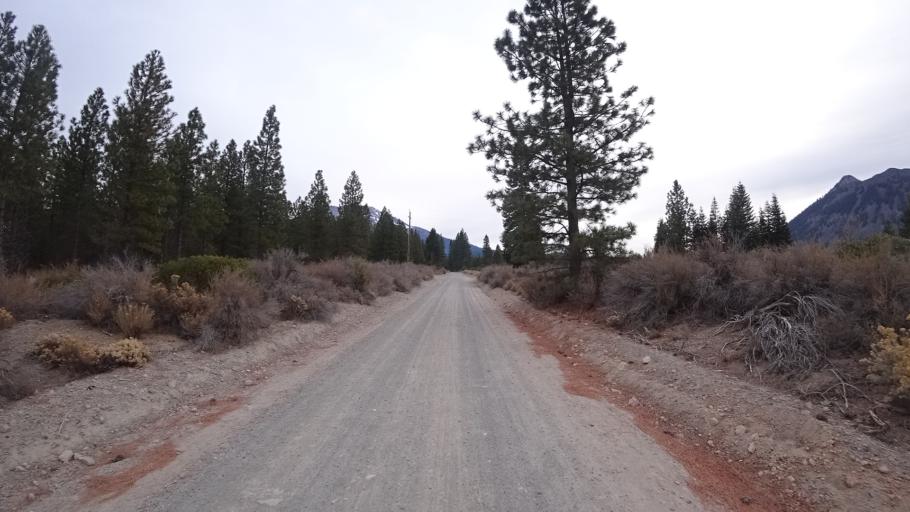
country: US
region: California
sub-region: Siskiyou County
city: Weed
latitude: 41.3930
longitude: -122.3653
